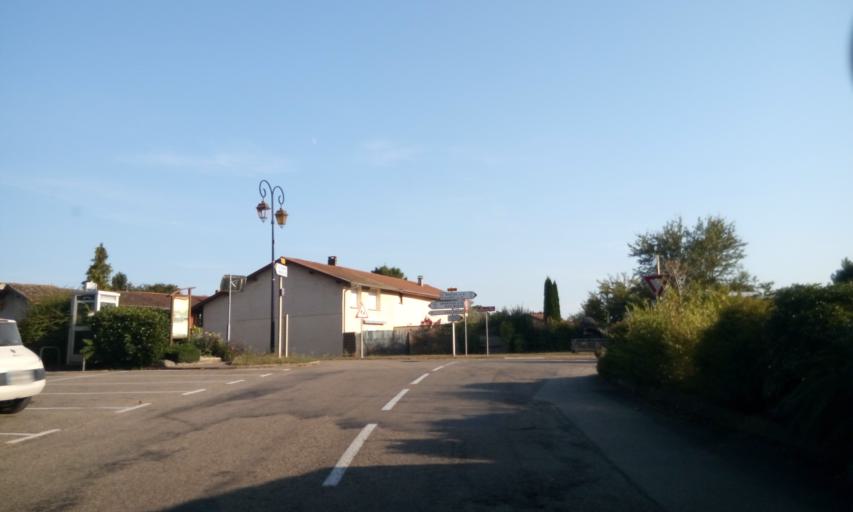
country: FR
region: Rhone-Alpes
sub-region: Departement de l'Ain
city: Chalamont
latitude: 45.9805
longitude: 5.1022
